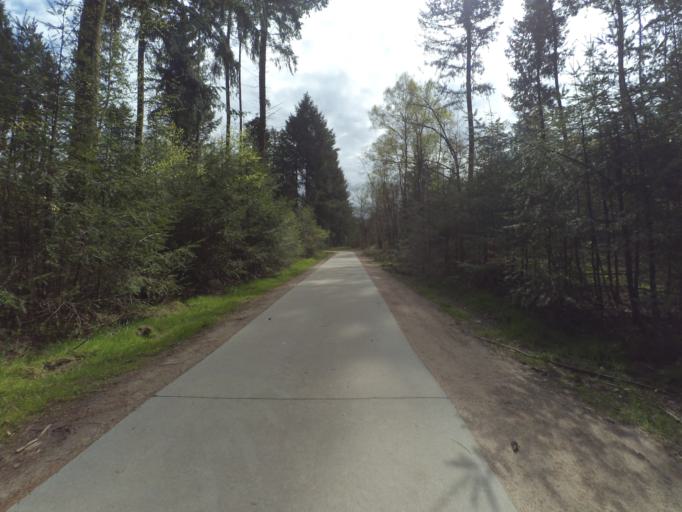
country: NL
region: Gelderland
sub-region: Gemeente Epe
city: Epe
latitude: 52.3718
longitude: 5.9698
